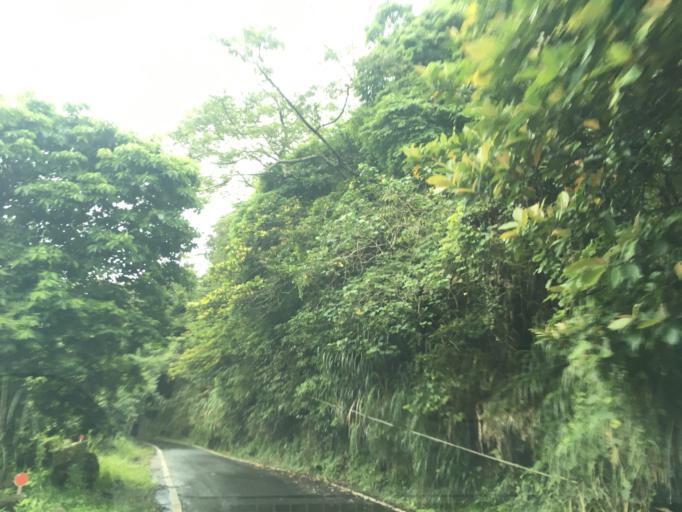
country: TW
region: Taiwan
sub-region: Yunlin
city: Douliu
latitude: 23.5603
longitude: 120.6548
